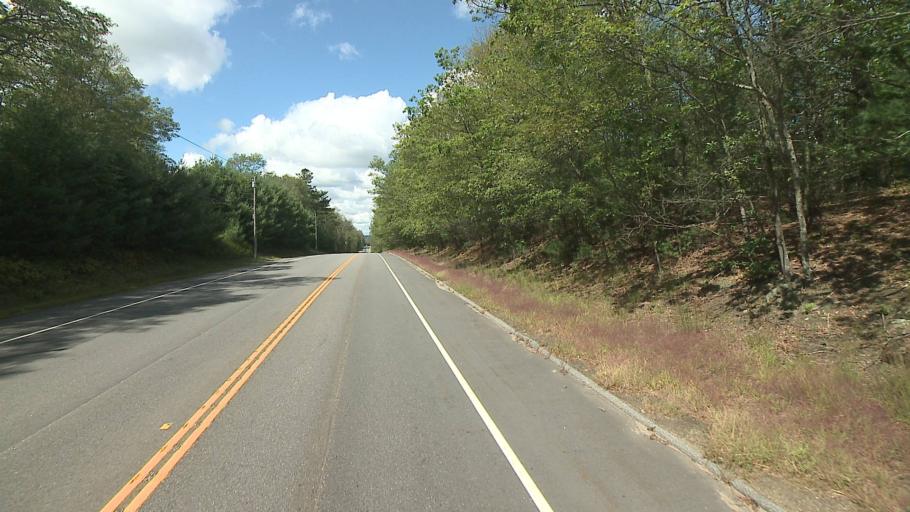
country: US
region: Connecticut
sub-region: Windham County
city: South Woodstock
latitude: 41.8724
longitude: -72.0630
